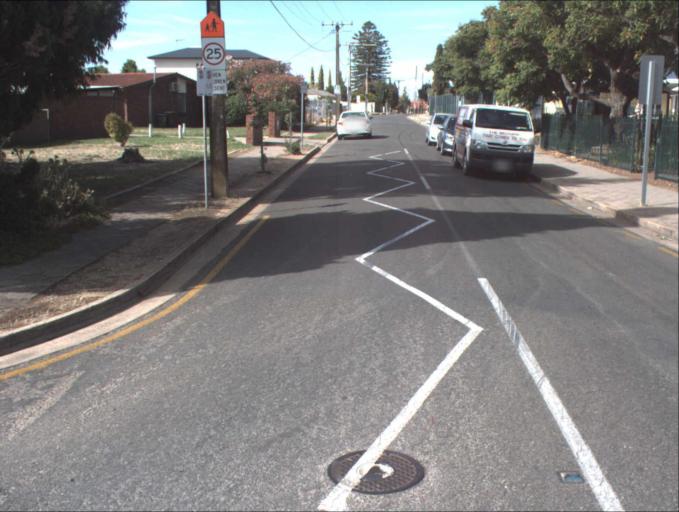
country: AU
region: South Australia
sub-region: Port Adelaide Enfield
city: Klemzig
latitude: -34.8685
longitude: 138.6424
